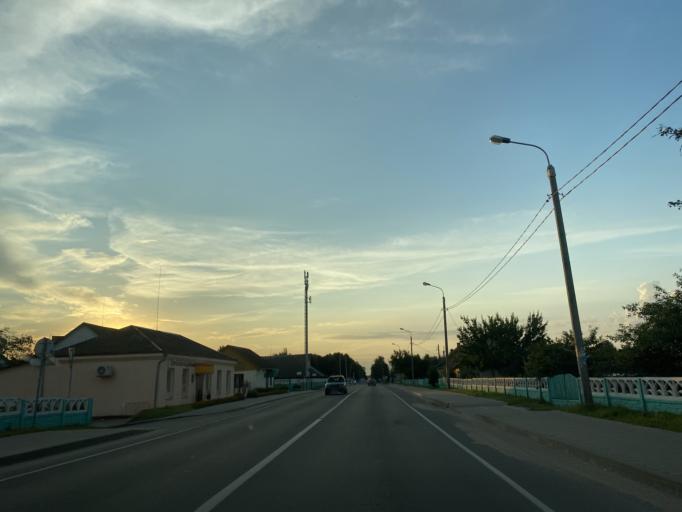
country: BY
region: Brest
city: Ivatsevichy
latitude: 52.7105
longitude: 25.3526
